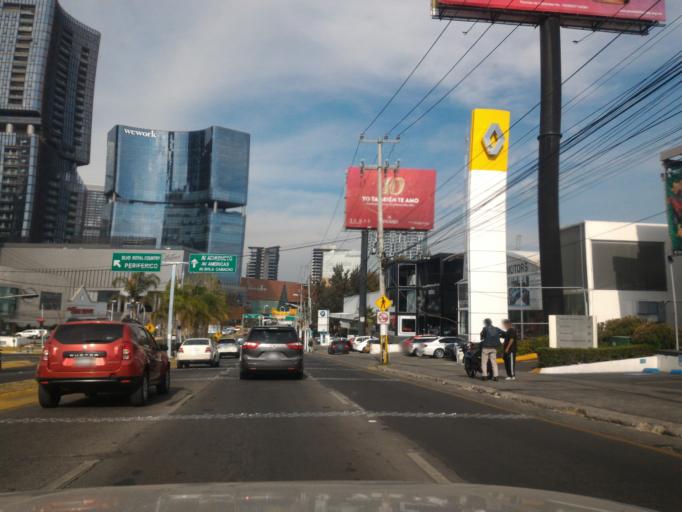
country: MX
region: Jalisco
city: Zapopan2
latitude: 20.7050
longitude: -103.4136
